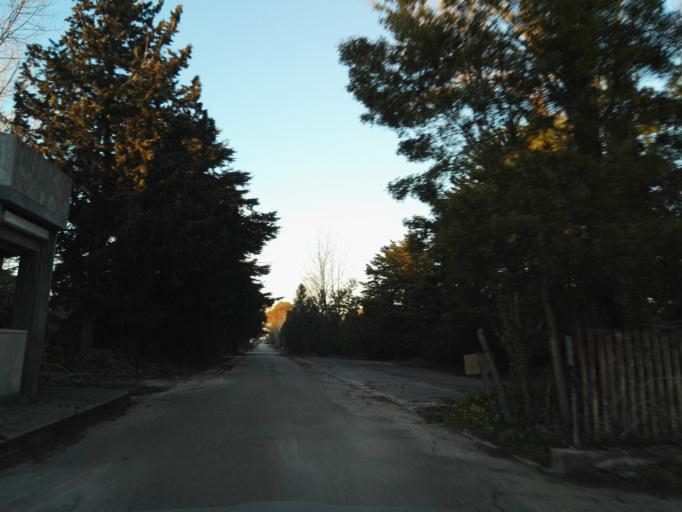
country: PT
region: Setubal
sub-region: Seixal
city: Corroios
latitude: 38.6220
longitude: -9.1460
